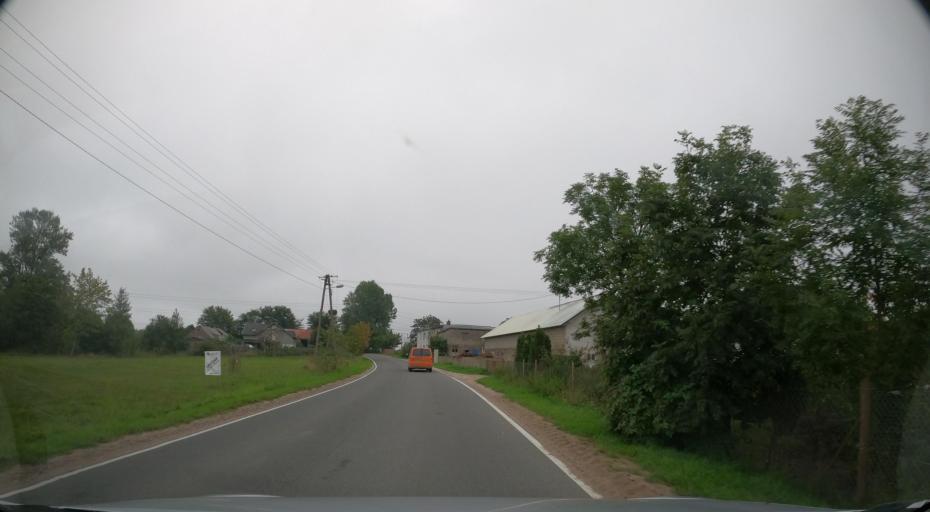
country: PL
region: Pomeranian Voivodeship
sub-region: Powiat wejherowski
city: Szemud
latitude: 54.5009
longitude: 18.1723
